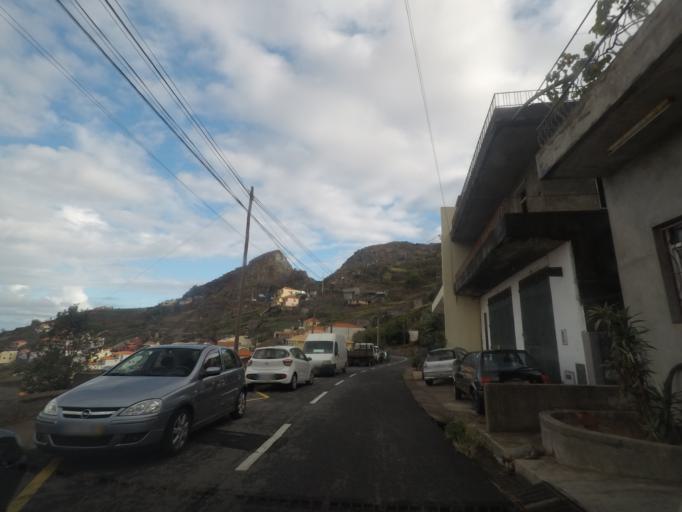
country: PT
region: Madeira
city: Camara de Lobos
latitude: 32.6577
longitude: -16.9971
